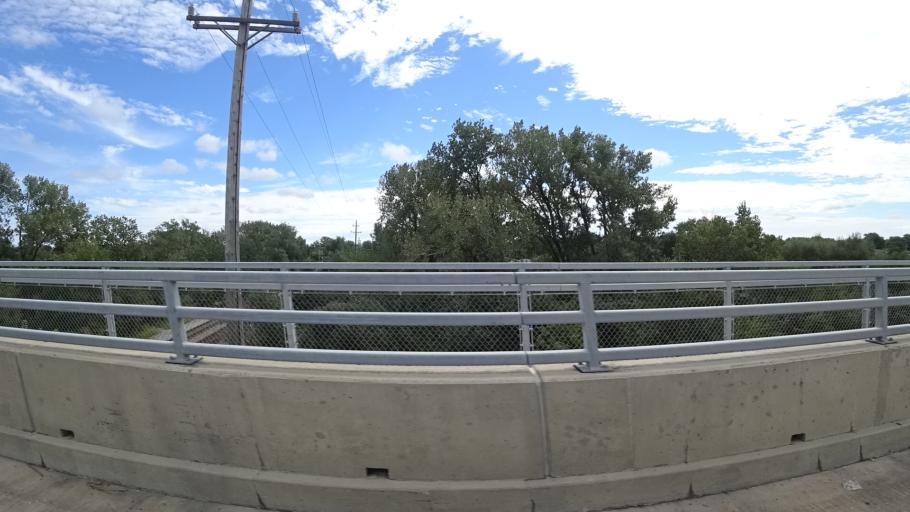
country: US
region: Illinois
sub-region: Cook County
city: Chicago Ridge
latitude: 41.7077
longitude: -87.7825
